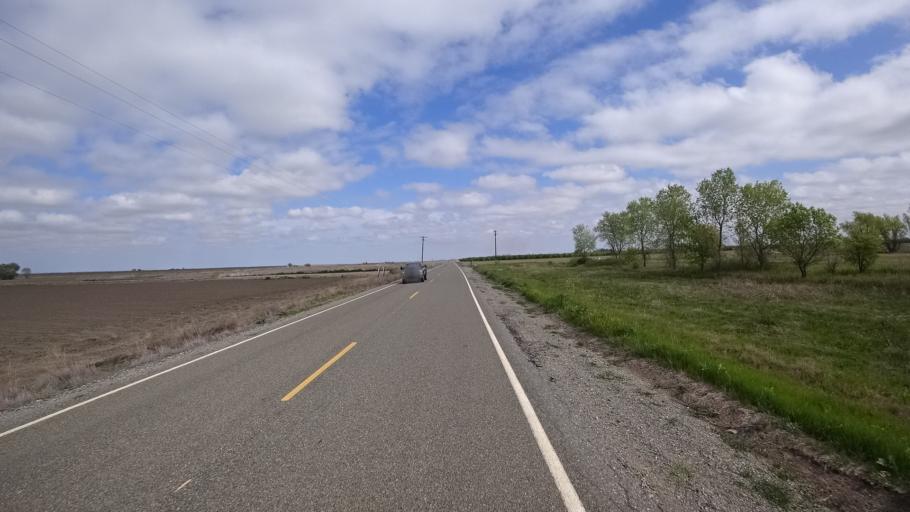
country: US
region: California
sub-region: Colusa County
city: Colusa
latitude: 39.4046
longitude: -121.9292
